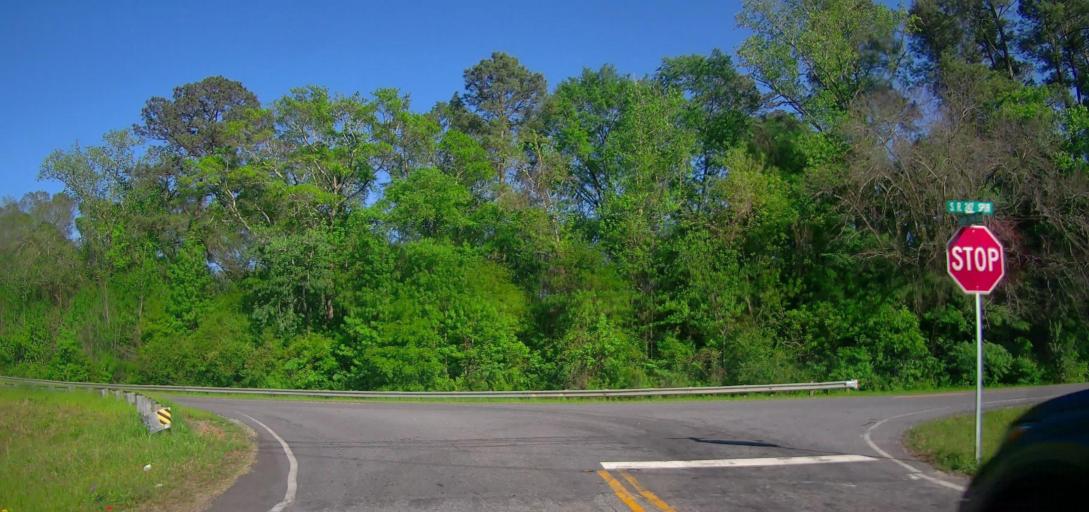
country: US
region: Georgia
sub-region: Houston County
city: Perry
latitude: 32.4498
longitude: -83.6259
